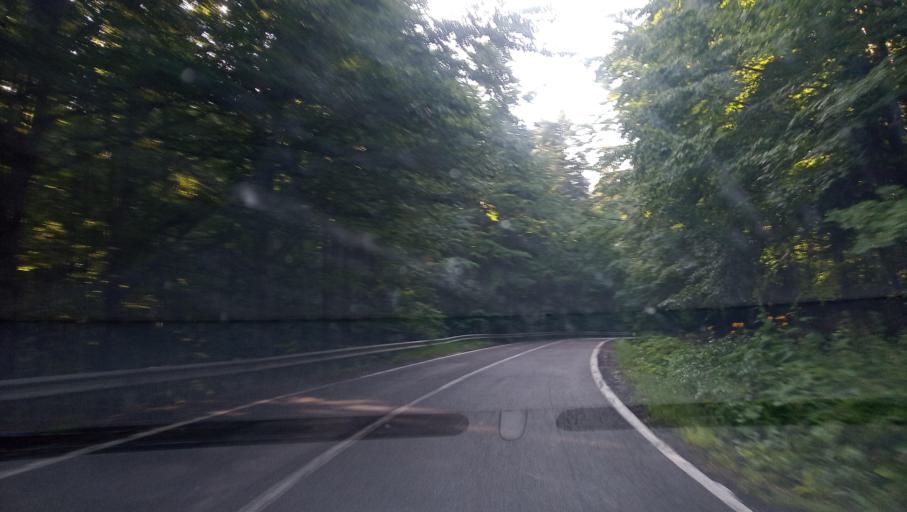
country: RO
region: Prahova
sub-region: Oras Sinaia
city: Sinaia
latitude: 45.3223
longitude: 25.5192
